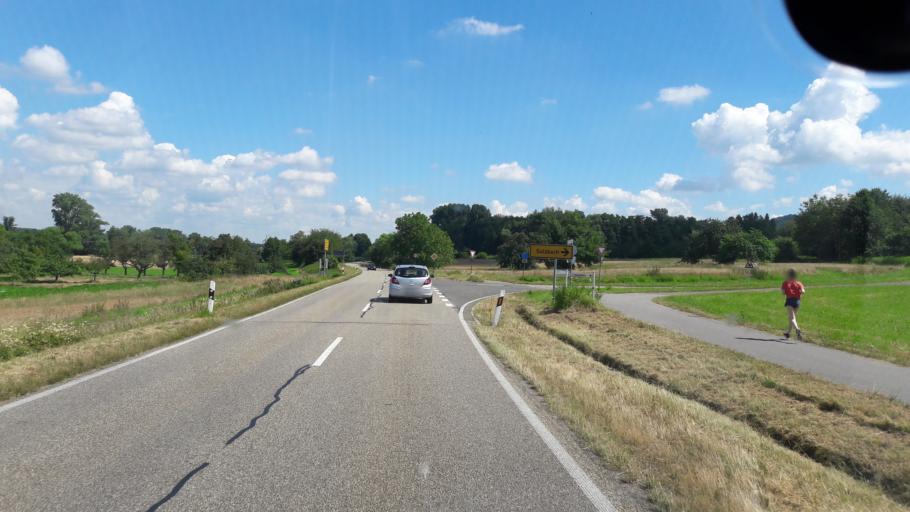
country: DE
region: Baden-Wuerttemberg
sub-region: Karlsruhe Region
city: Malsch
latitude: 48.8959
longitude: 8.3574
